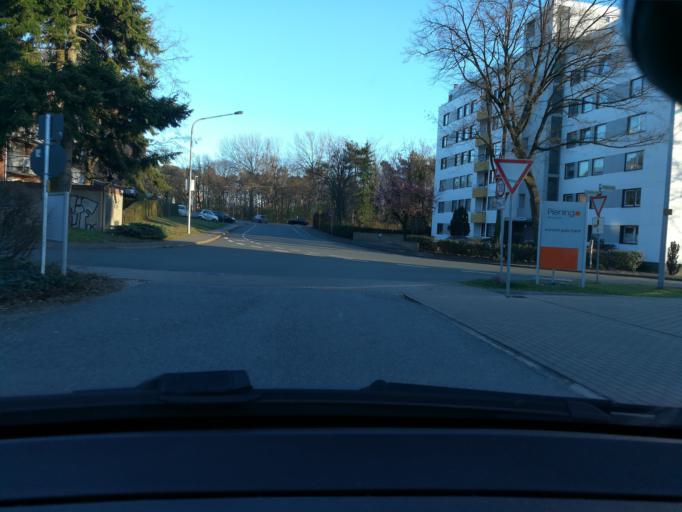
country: DE
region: North Rhine-Westphalia
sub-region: Regierungsbezirk Detmold
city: Oerlinghausen
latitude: 51.9445
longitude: 8.5798
